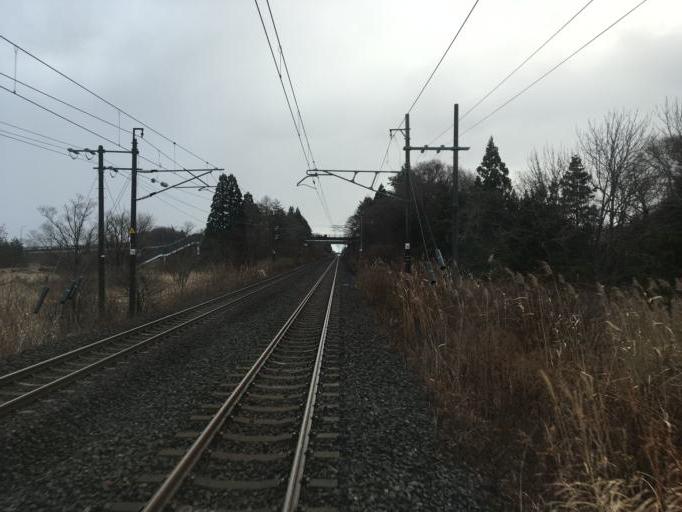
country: JP
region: Aomori
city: Aomori Shi
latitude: 40.9312
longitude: 140.9665
